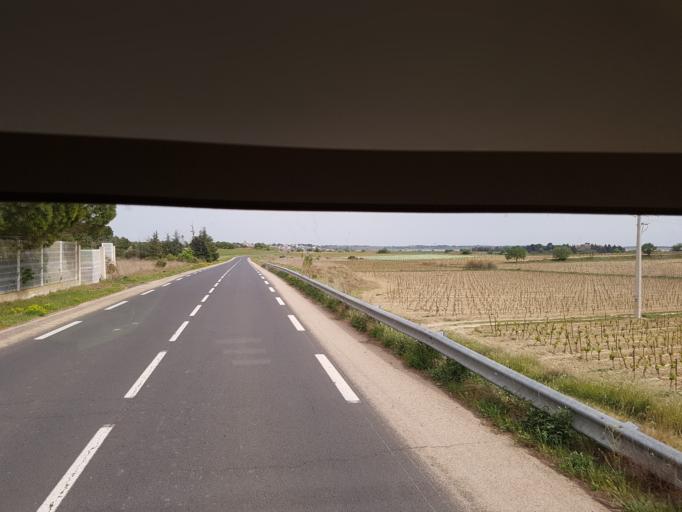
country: FR
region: Languedoc-Roussillon
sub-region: Departement de l'Herault
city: Vendres
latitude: 43.2753
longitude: 3.1997
